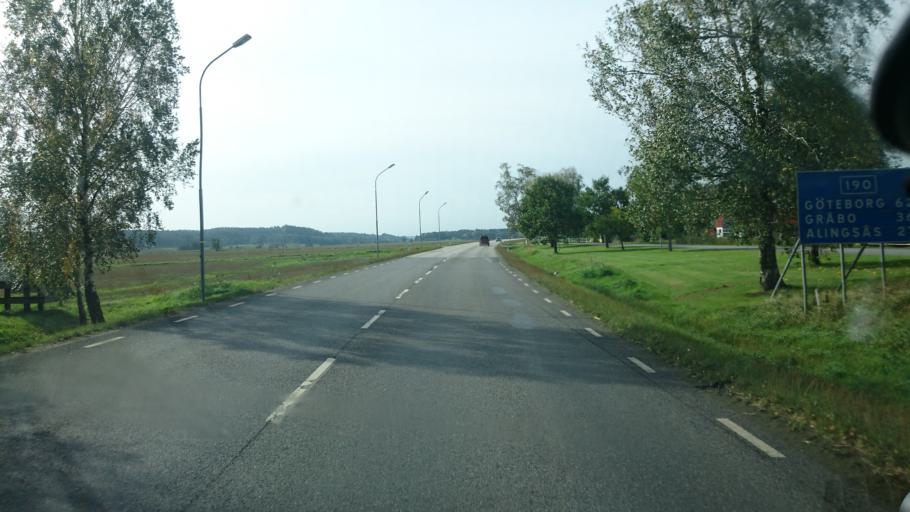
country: SE
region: Vaestra Goetaland
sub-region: Alingsas Kommun
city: Sollebrunn
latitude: 58.1164
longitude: 12.5323
